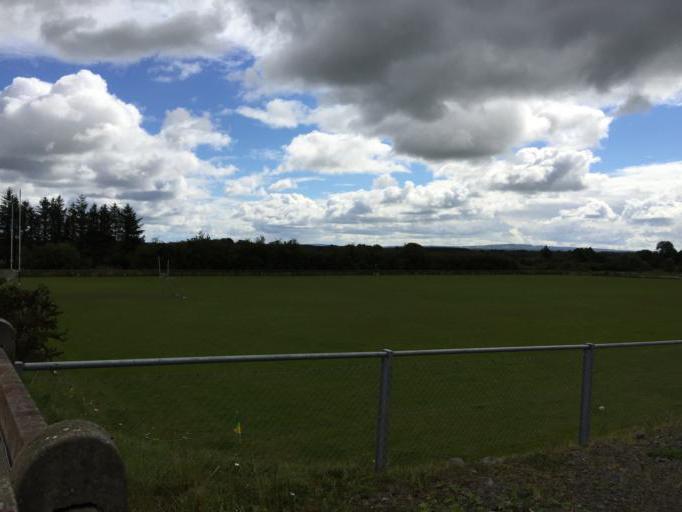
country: IE
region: Connaught
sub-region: Sligo
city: Tobercurry
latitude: 54.0370
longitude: -8.8474
